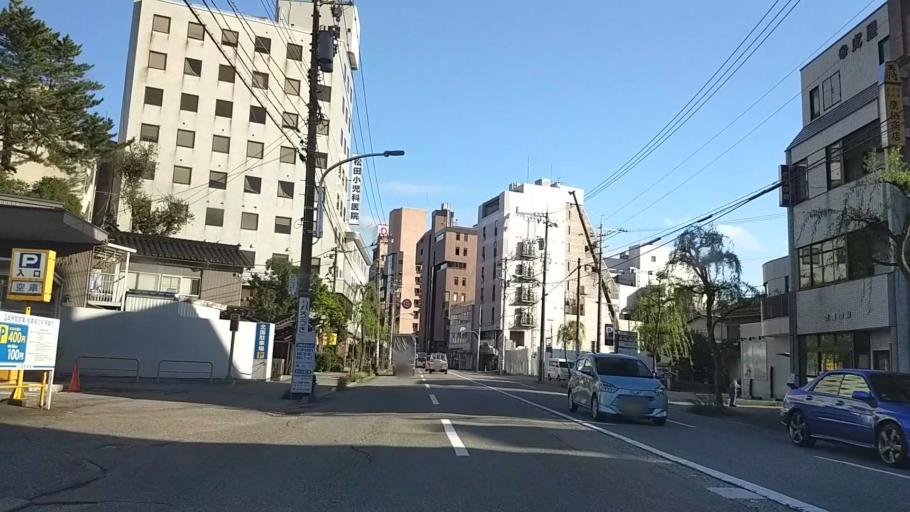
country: JP
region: Ishikawa
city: Kanazawa-shi
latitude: 36.5616
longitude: 136.6504
